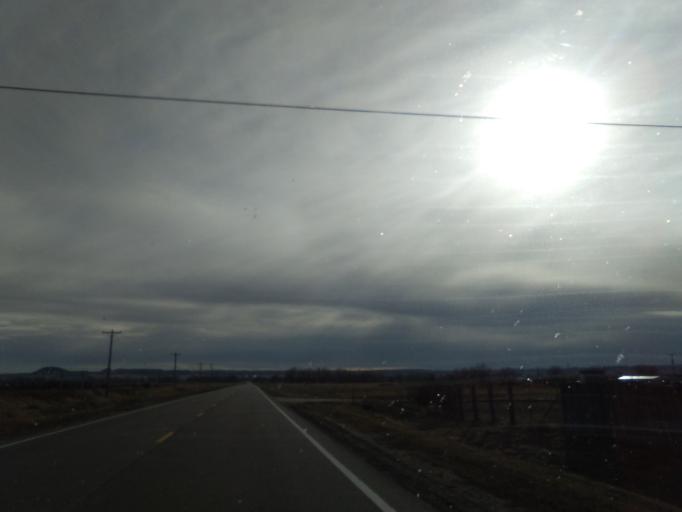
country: US
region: Nebraska
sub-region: Scotts Bluff County
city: Gering
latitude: 41.8068
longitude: -103.5193
